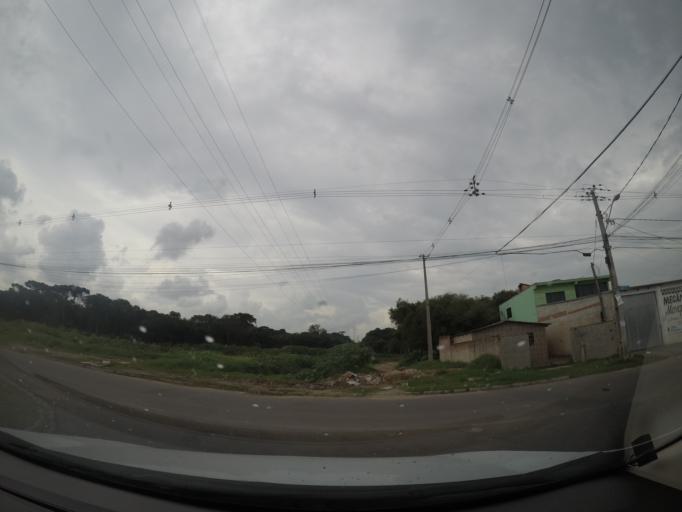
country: BR
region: Parana
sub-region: Sao Jose Dos Pinhais
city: Sao Jose dos Pinhais
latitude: -25.5565
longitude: -49.2444
